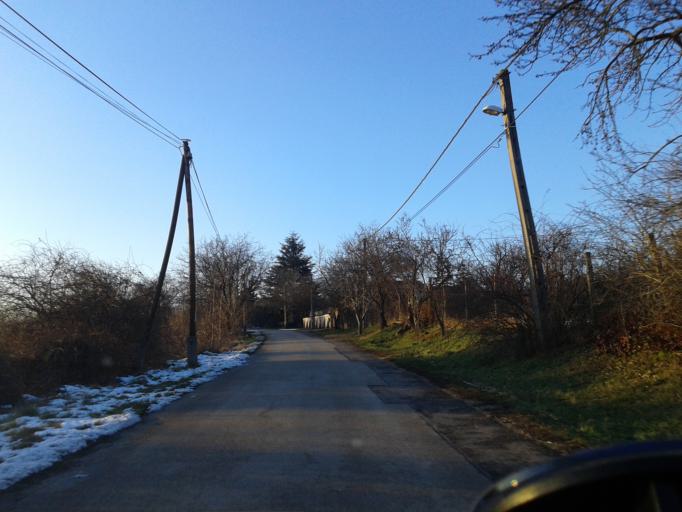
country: HU
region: Pest
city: Diosd
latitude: 47.4130
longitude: 18.9636
